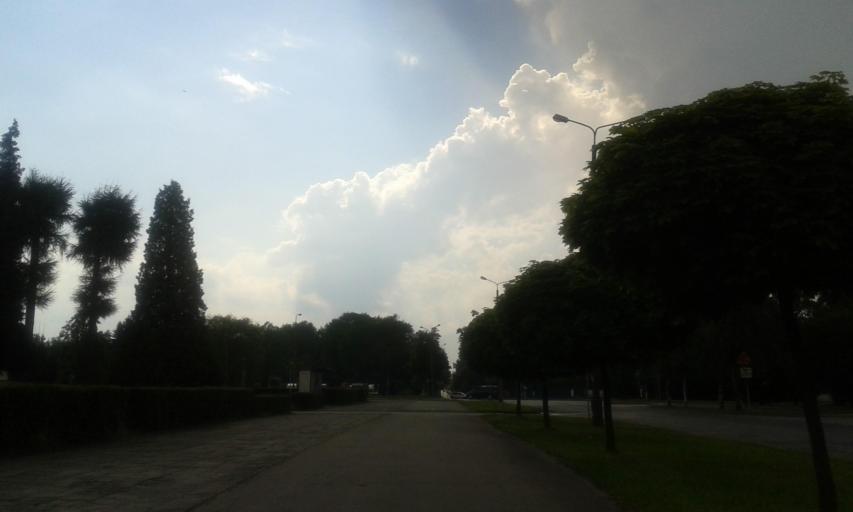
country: PL
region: Lesser Poland Voivodeship
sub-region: Powiat oswiecimski
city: Zaborze
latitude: 50.0353
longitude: 19.2549
